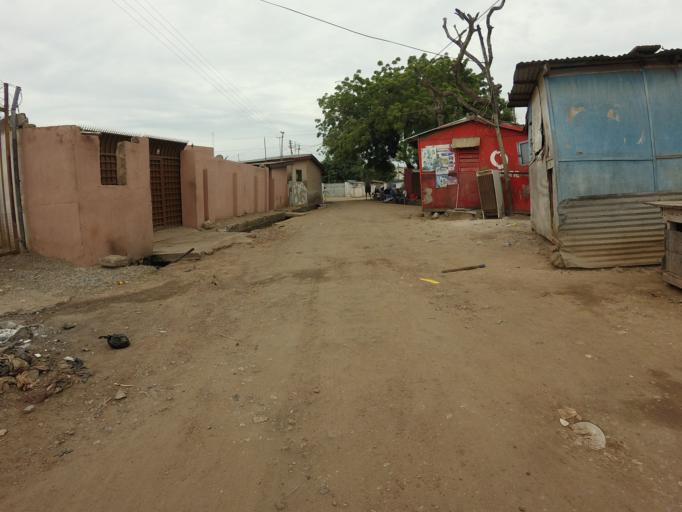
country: GH
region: Greater Accra
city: Accra
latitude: 5.5889
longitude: -0.2164
